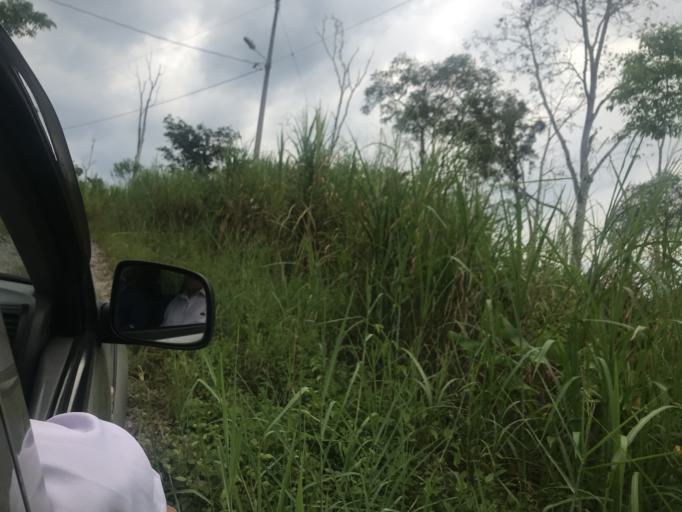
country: EC
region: Napo
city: Tena
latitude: -1.0232
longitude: -77.7424
